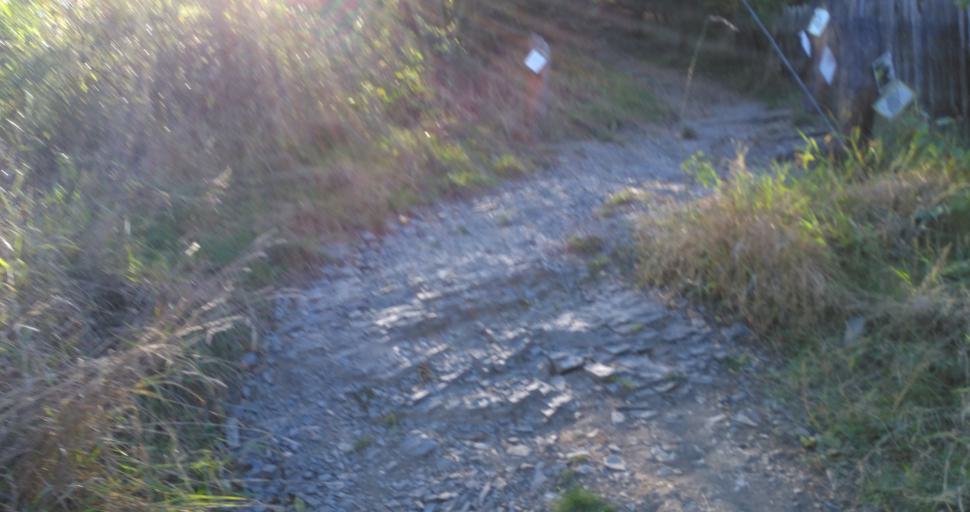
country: CZ
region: Central Bohemia
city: Pavlikov
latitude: 49.9688
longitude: 13.7739
